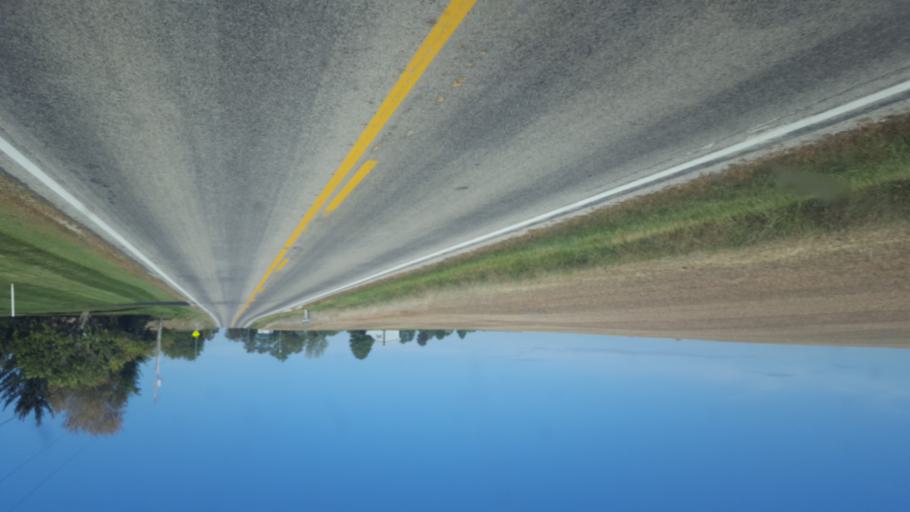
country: US
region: Ohio
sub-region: Crawford County
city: Bucyrus
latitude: 40.9006
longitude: -83.0167
